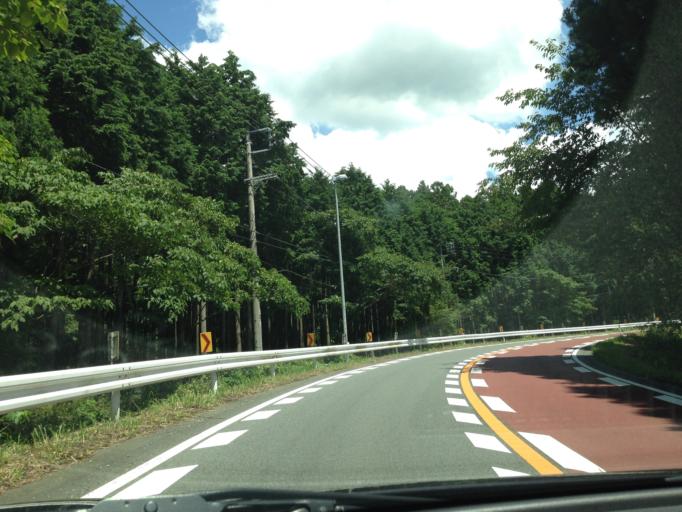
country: JP
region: Shizuoka
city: Fuji
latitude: 35.2231
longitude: 138.7317
